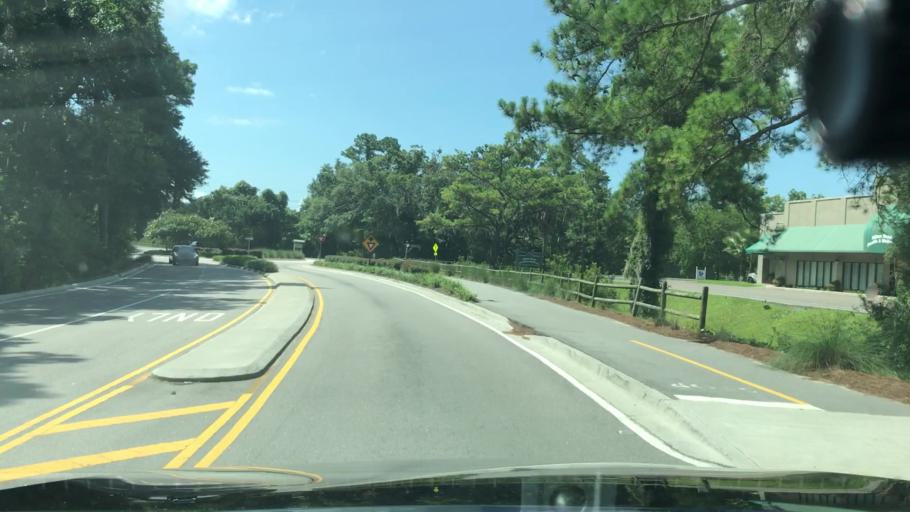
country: US
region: South Carolina
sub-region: Beaufort County
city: Hilton Head Island
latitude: 32.2065
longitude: -80.7027
